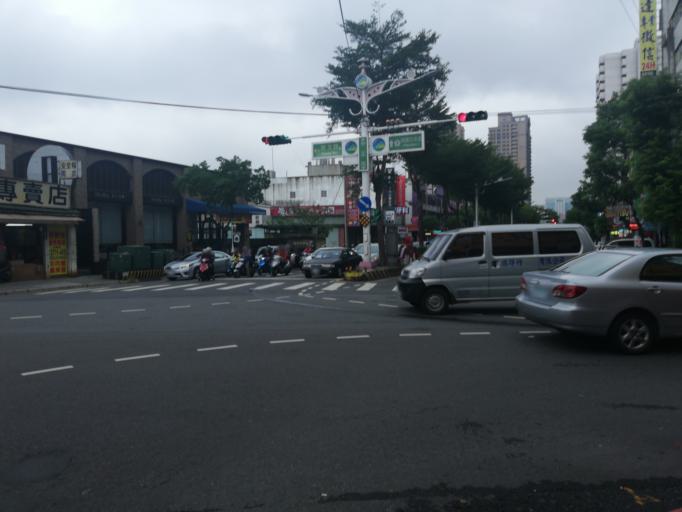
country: TW
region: Taiwan
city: Taoyuan City
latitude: 25.0074
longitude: 121.3030
